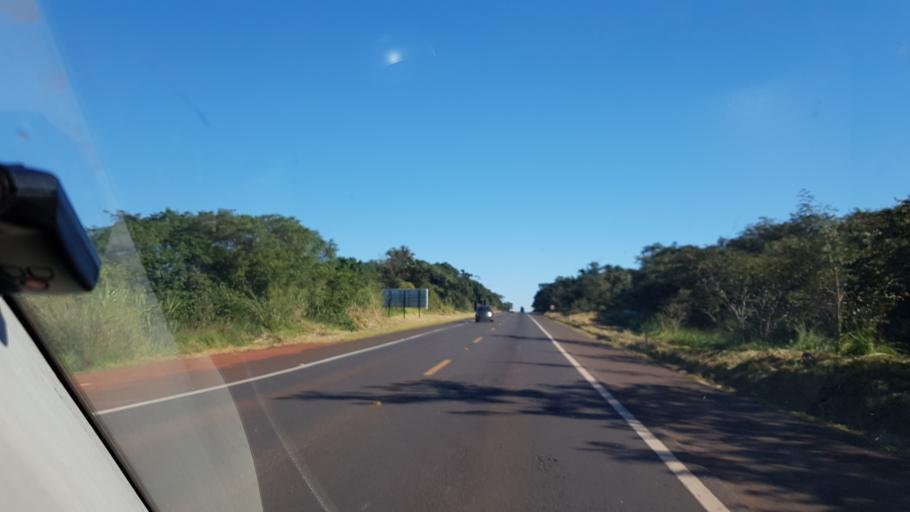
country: BR
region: Sao Paulo
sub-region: Assis
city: Assis
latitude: -22.5886
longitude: -50.4958
